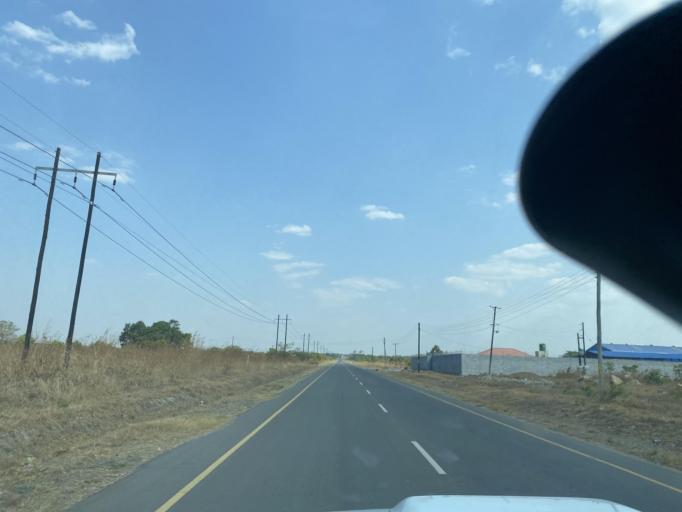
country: ZM
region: Lusaka
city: Lusaka
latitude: -15.3216
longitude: 28.0637
